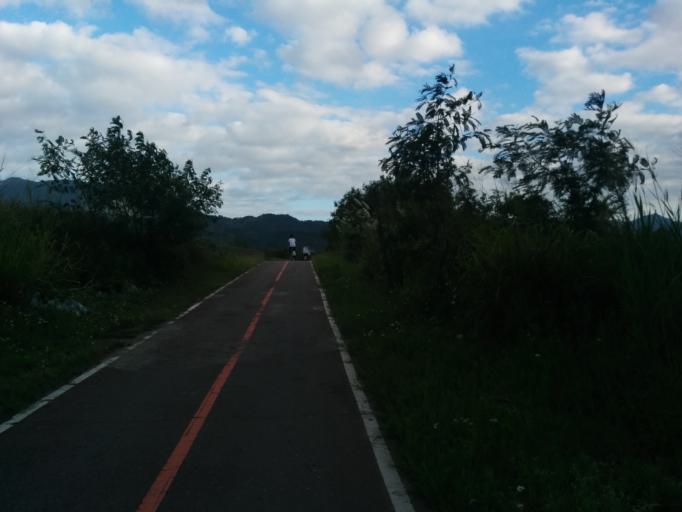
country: TW
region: Taiwan
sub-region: Taitung
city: Taitung
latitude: 23.0274
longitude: 121.1586
